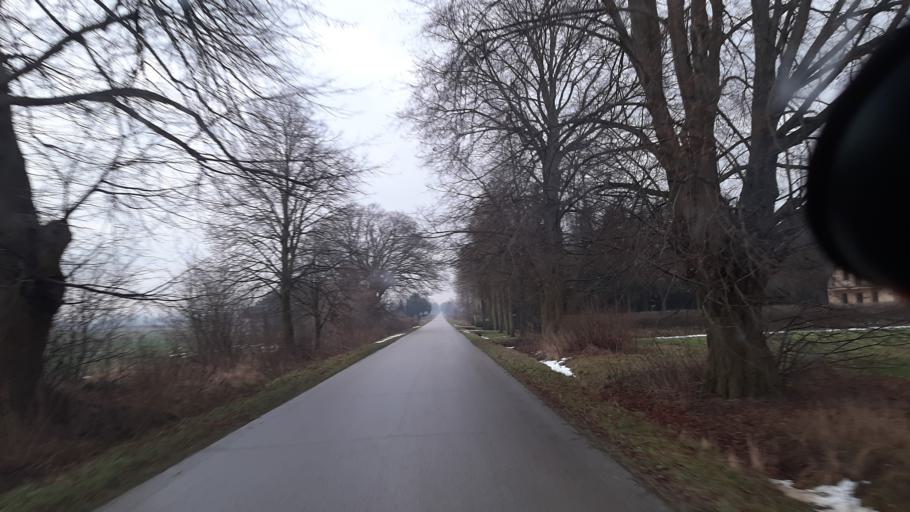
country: PL
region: Lublin Voivodeship
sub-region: Powiat lubelski
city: Lublin
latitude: 51.3400
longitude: 22.5375
